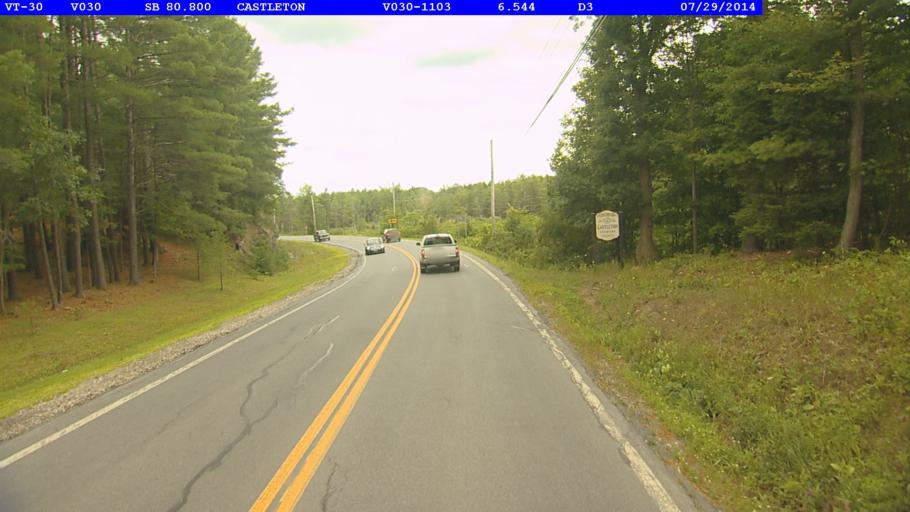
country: US
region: Vermont
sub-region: Rutland County
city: Castleton
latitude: 43.6789
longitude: -73.1910
